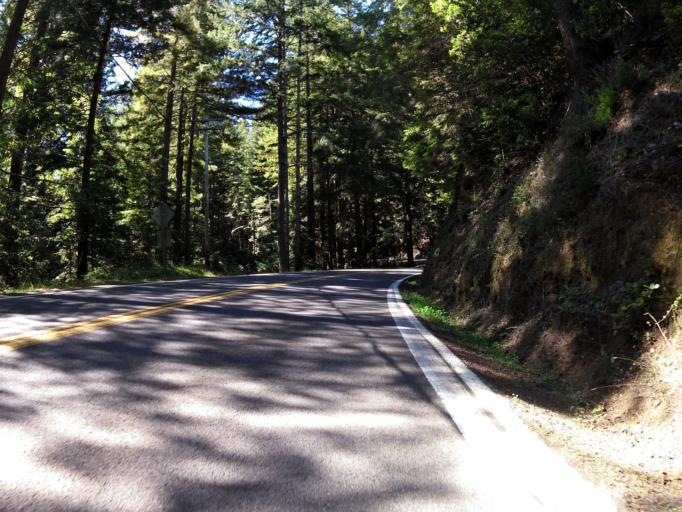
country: US
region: California
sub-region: Mendocino County
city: Fort Bragg
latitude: 39.7315
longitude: -123.8097
